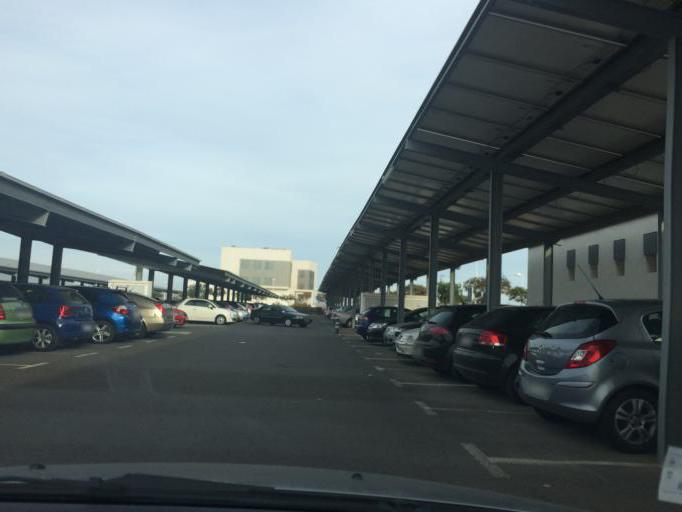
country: ES
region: Andalusia
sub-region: Provincia de Almeria
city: Almeria
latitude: 36.8314
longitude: -2.4025
